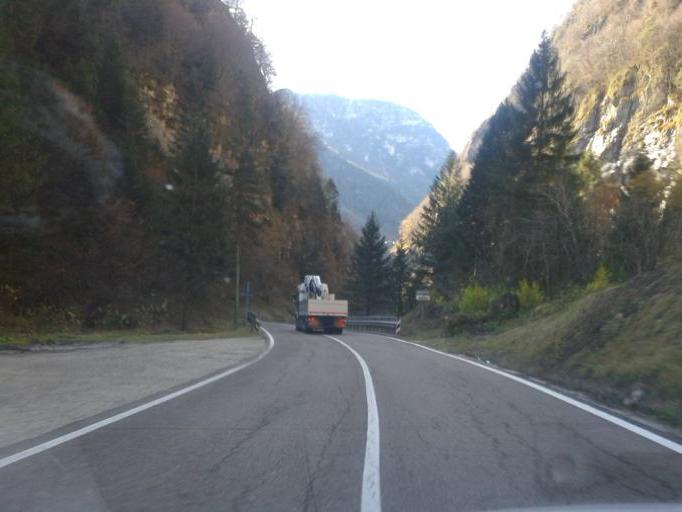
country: IT
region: Trentino-Alto Adige
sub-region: Provincia di Trento
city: Condino
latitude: 45.8588
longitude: 10.6377
